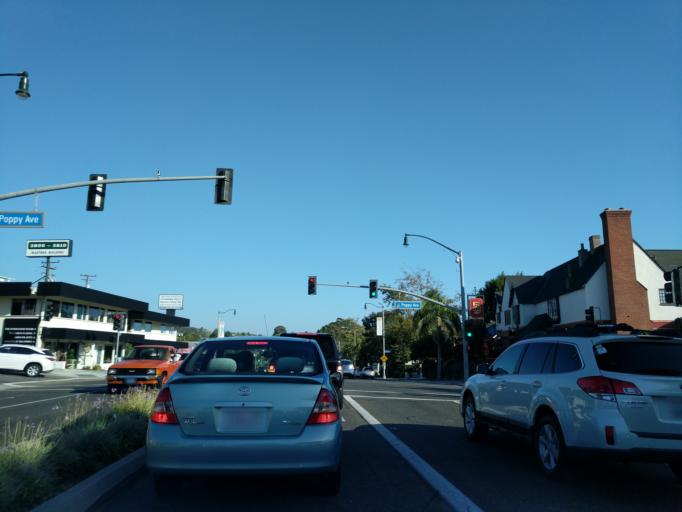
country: US
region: California
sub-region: Orange County
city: San Joaquin Hills
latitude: 33.5939
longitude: -117.8672
